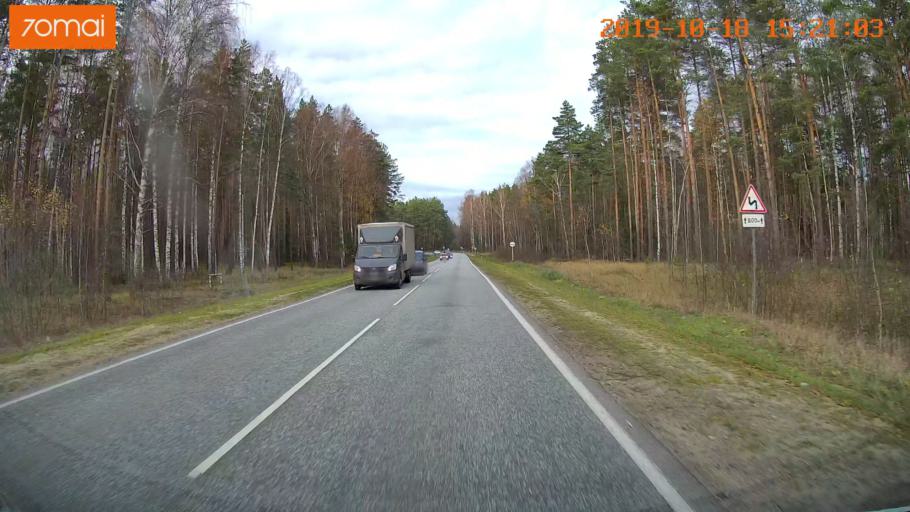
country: RU
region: Vladimir
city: Anopino
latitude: 55.6939
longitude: 40.7489
